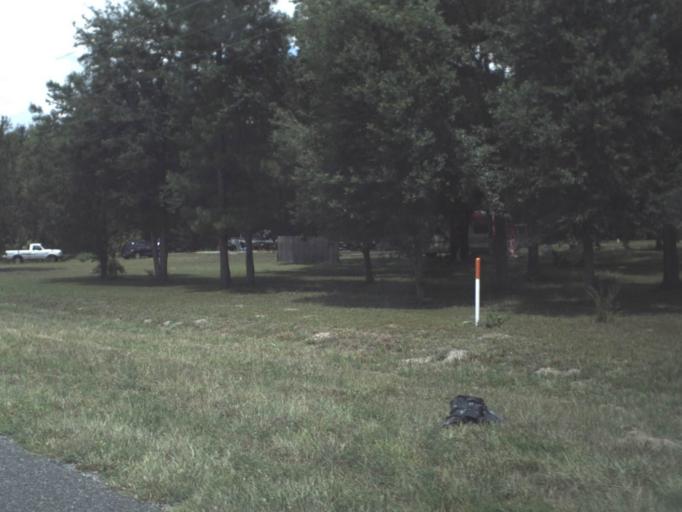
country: US
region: Florida
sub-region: Taylor County
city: Perry
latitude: 30.0222
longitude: -83.5344
